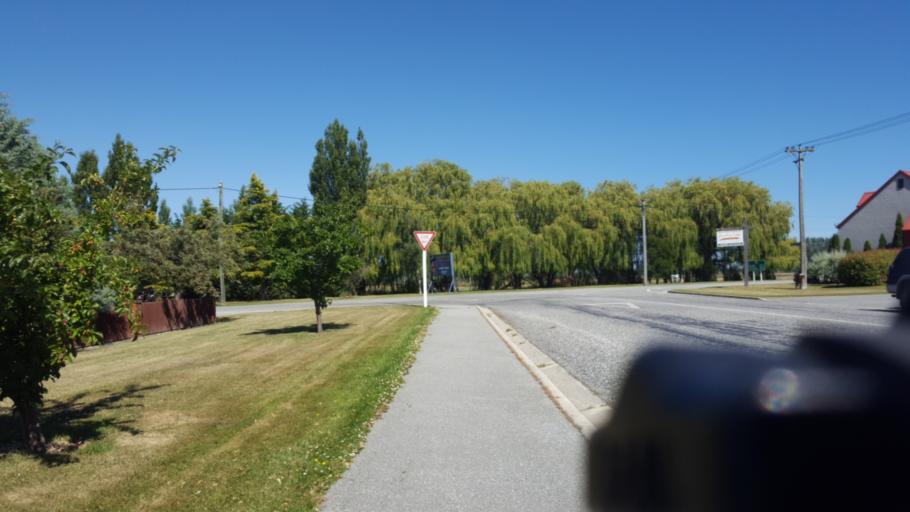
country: NZ
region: Otago
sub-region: Dunedin City
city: Dunedin
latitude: -45.1268
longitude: 170.0967
